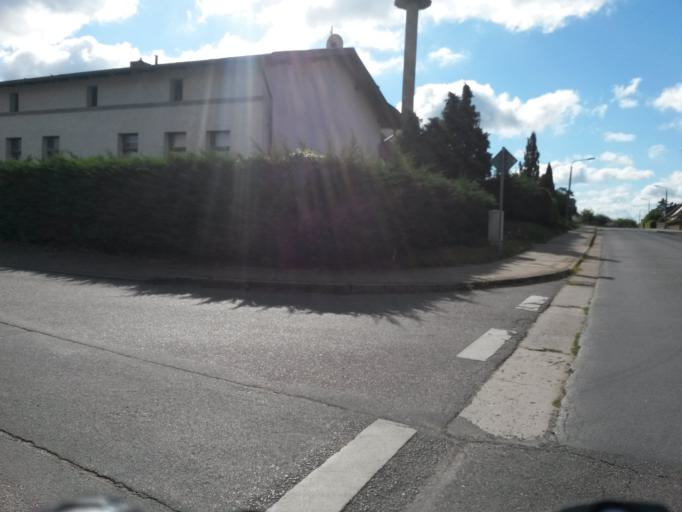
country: DE
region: Brandenburg
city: Templin
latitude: 53.1137
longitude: 13.4992
